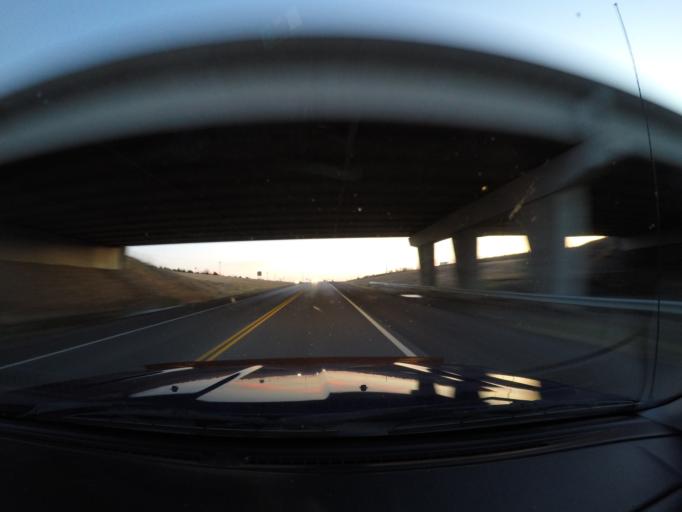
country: US
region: Kansas
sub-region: Douglas County
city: Lawrence
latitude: 38.9717
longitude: -95.3343
